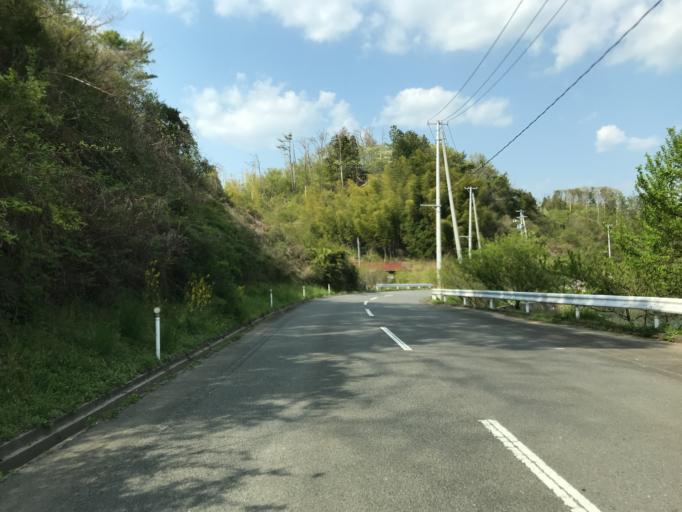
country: JP
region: Fukushima
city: Iwaki
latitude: 36.9934
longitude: 140.7662
